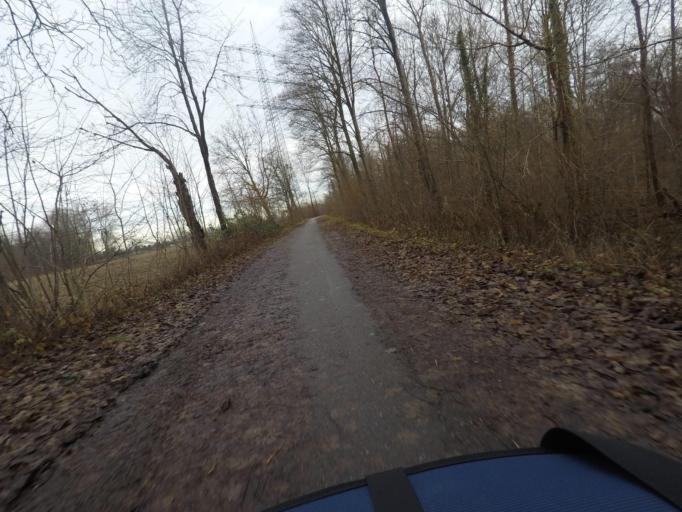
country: DE
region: Baden-Wuerttemberg
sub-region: Karlsruhe Region
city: Rheinau
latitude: 48.8711
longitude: 8.1727
